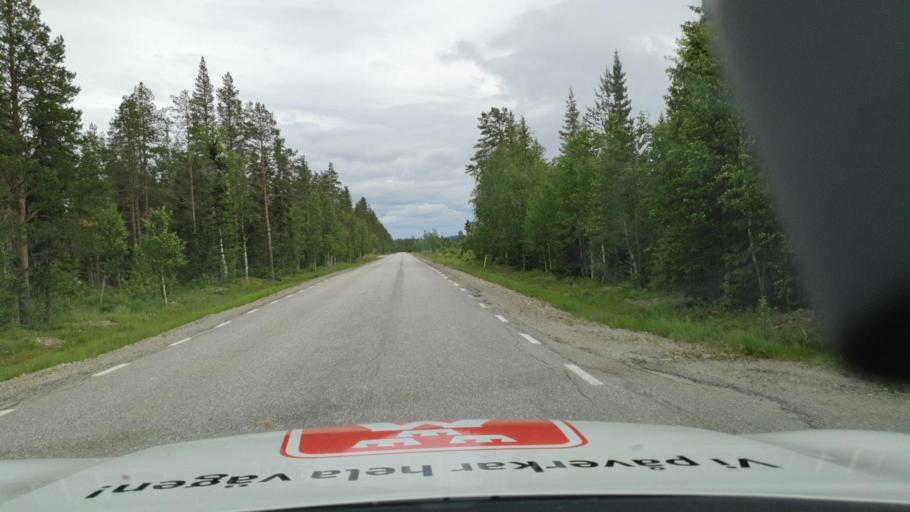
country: SE
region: Vaesterbotten
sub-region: Lycksele Kommun
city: Soderfors
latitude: 64.3438
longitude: 18.1369
